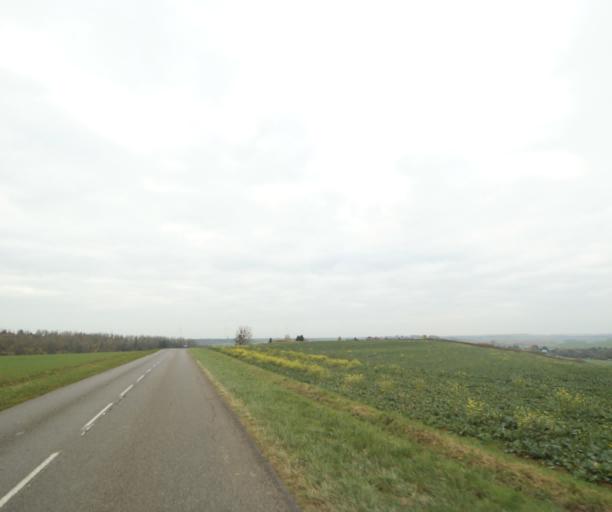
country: FR
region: Lorraine
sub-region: Departement de Meurthe-et-Moselle
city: Mancieulles
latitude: 49.2921
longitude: 5.9069
